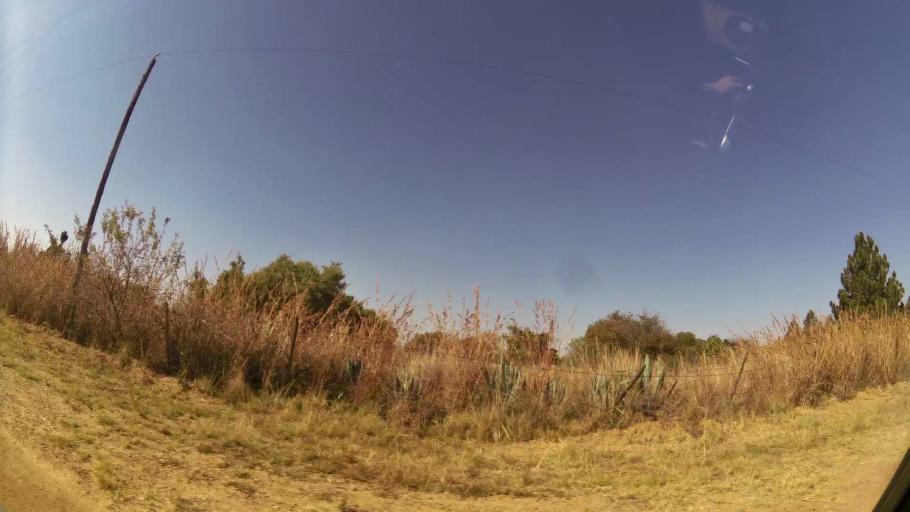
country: ZA
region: Gauteng
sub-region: City of Johannesburg Metropolitan Municipality
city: Diepsloot
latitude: -25.9274
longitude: 28.0754
